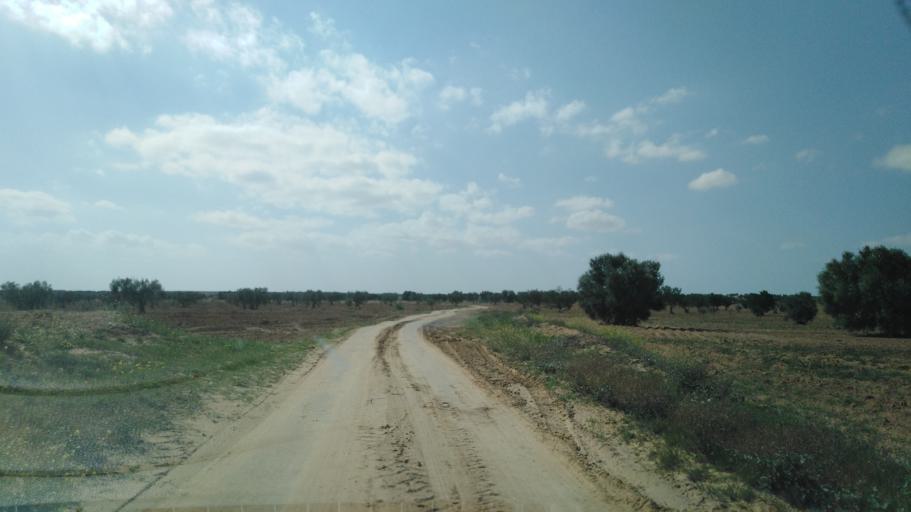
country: TN
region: Safaqis
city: Bi'r `Ali Bin Khalifah
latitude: 34.7981
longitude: 10.3877
